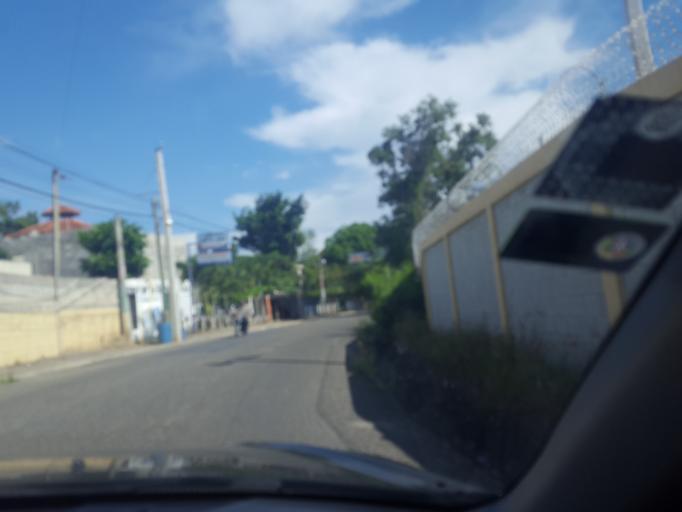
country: DO
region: La Vega
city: Rio Verde Arriba
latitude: 19.3669
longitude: -70.6053
